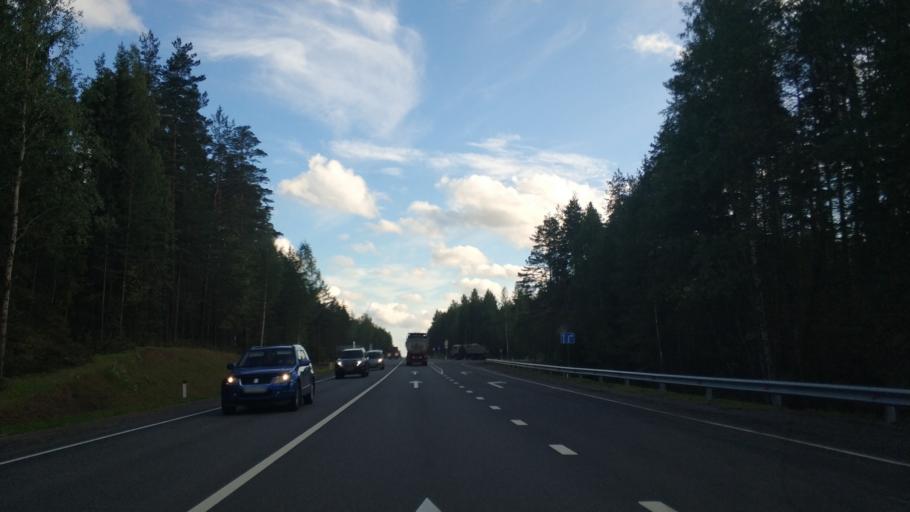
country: RU
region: Leningrad
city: Priozersk
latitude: 60.8731
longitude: 30.1624
